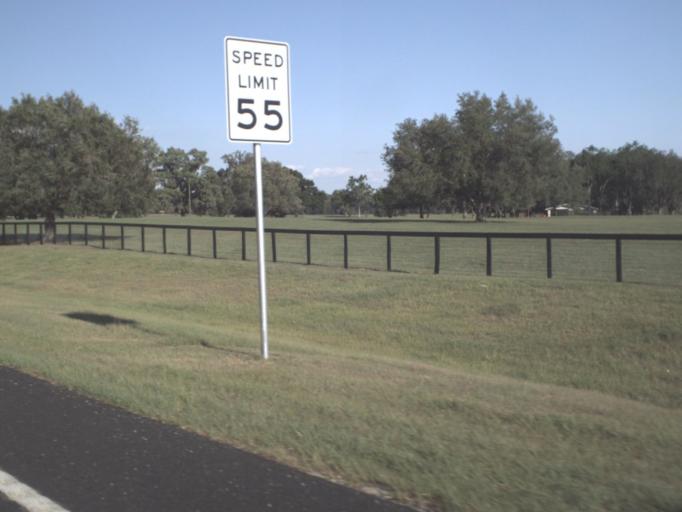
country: US
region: Florida
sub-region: Marion County
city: Ocala
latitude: 29.1867
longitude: -82.2999
